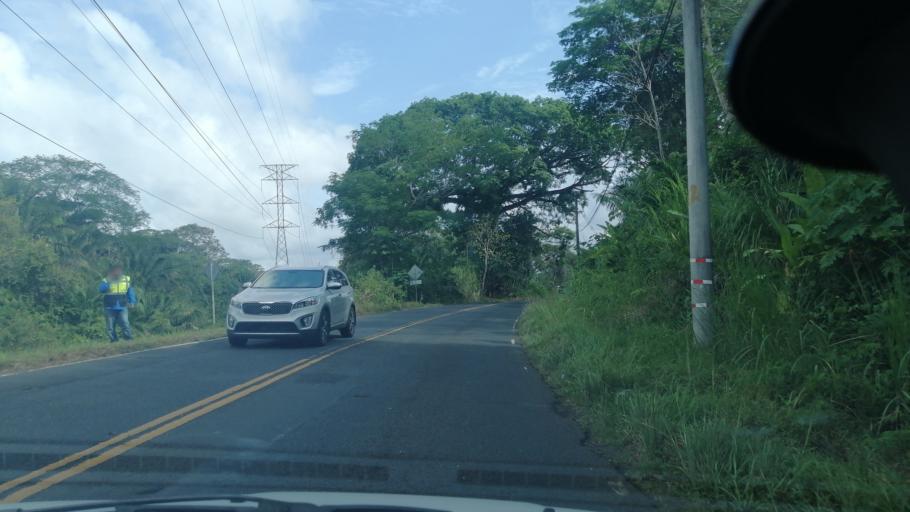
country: PA
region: Panama
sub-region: Distrito de Panama
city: Paraiso
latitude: 9.0481
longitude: -79.6370
